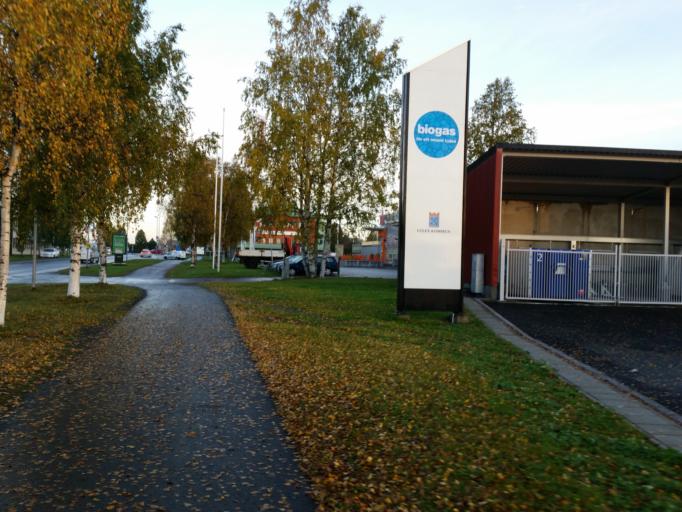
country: SE
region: Norrbotten
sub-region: Lulea Kommun
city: Lulea
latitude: 65.6016
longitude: 22.1396
